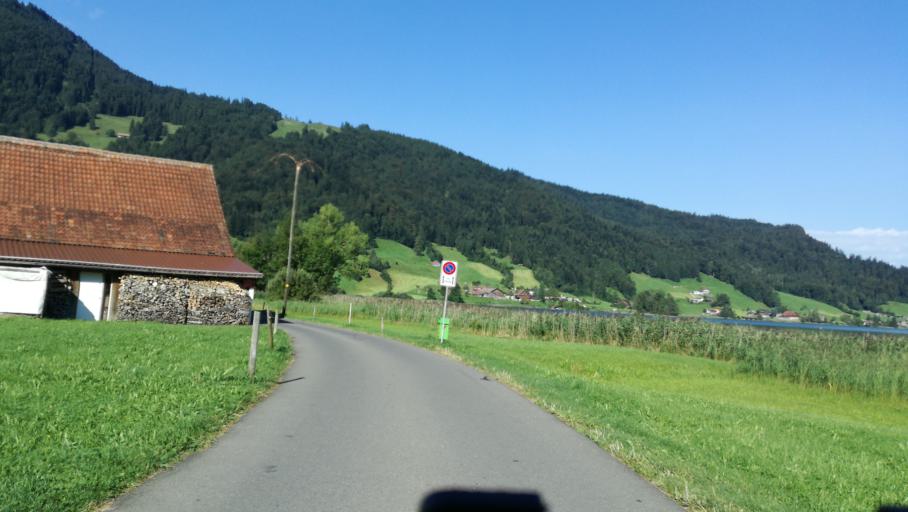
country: CH
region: Schwyz
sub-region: Bezirk Schwyz
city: Sattel
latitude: 47.1029
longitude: 8.6387
